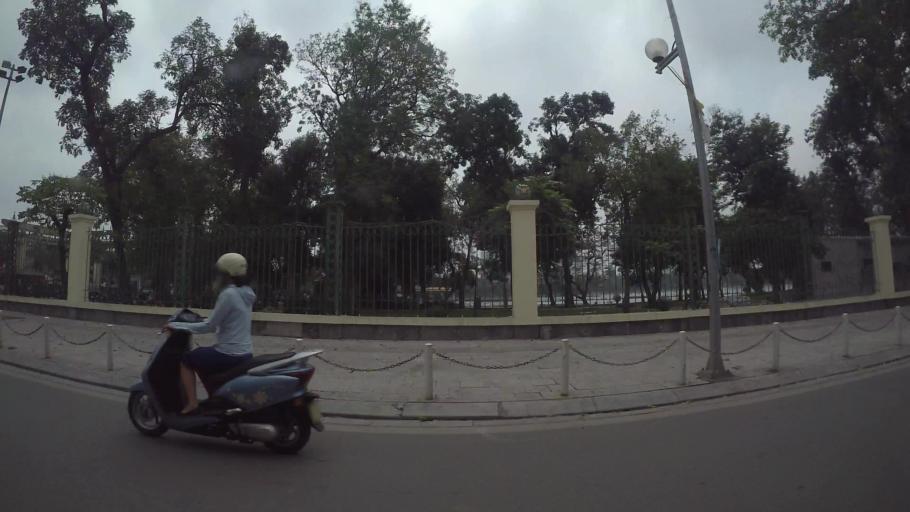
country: VN
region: Ha Noi
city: Hai BaTrung
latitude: 21.0087
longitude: 105.8460
